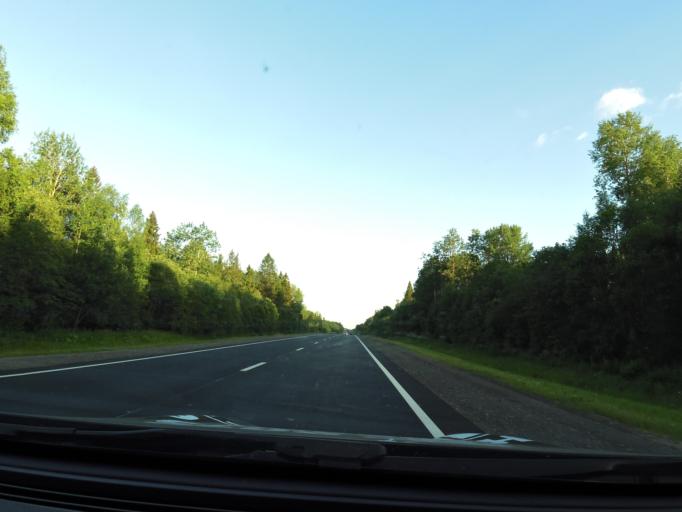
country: RU
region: Vologda
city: Gryazovets
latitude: 58.9109
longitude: 40.1792
